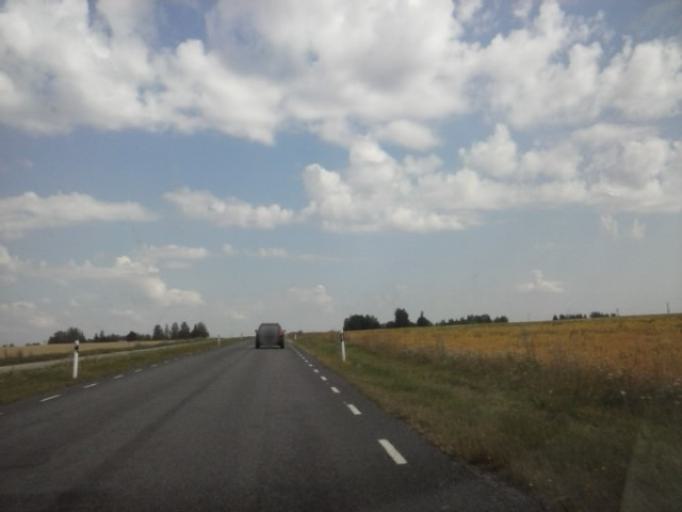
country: EE
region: Jogevamaa
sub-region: Tabivere vald
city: Tabivere
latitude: 58.5115
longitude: 26.6838
